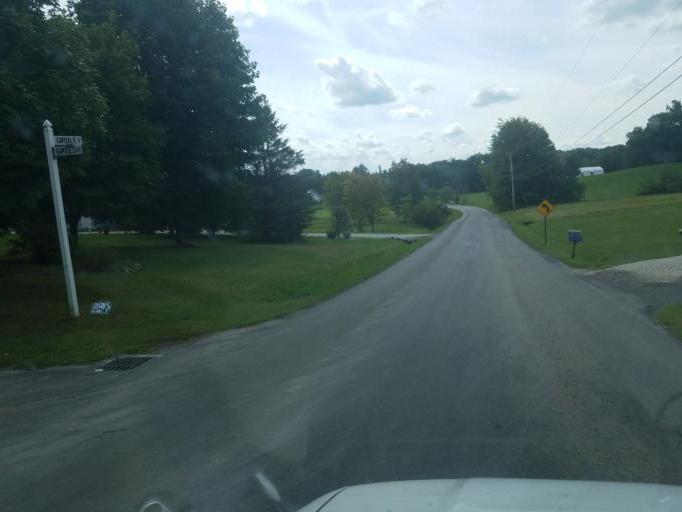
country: US
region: Ohio
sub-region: Geauga County
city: Middlefield
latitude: 41.4477
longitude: -80.9753
